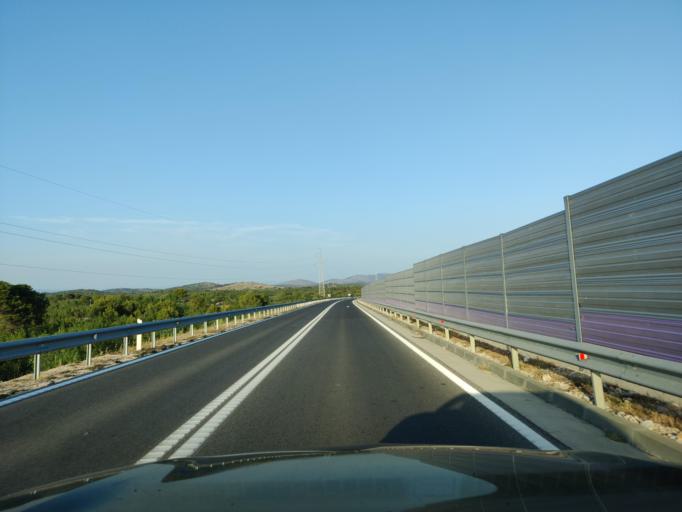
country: HR
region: Sibensko-Kniniska
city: Vodice
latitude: 43.7753
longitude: 15.7795
